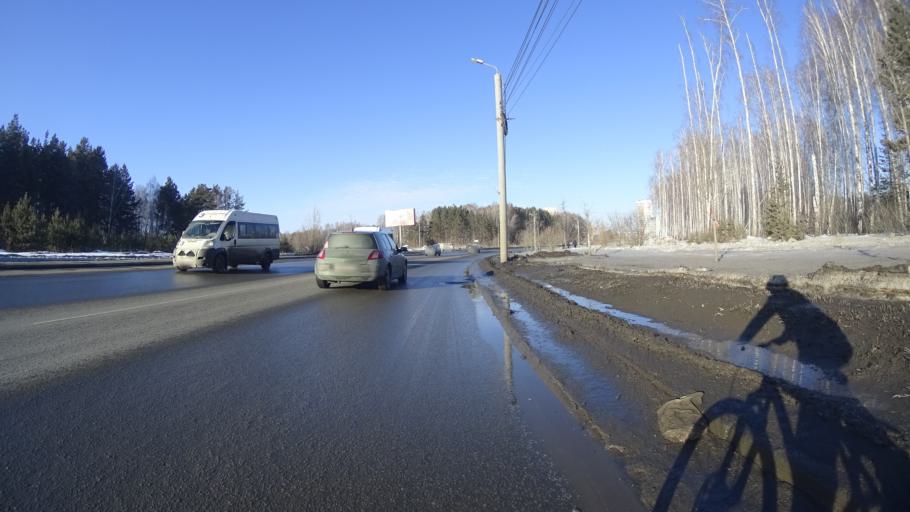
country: RU
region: Chelyabinsk
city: Roshchino
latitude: 55.1990
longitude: 61.2803
